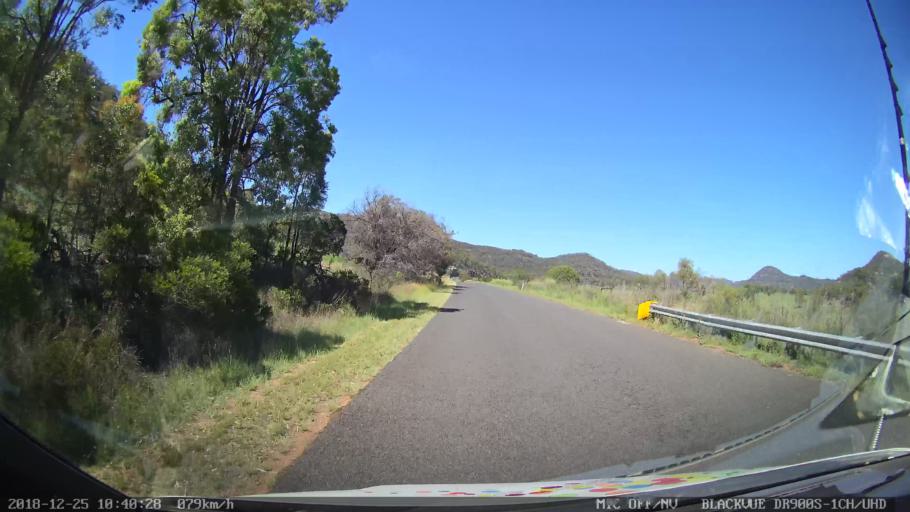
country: AU
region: New South Wales
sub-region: Upper Hunter Shire
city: Merriwa
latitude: -32.4079
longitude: 150.3430
